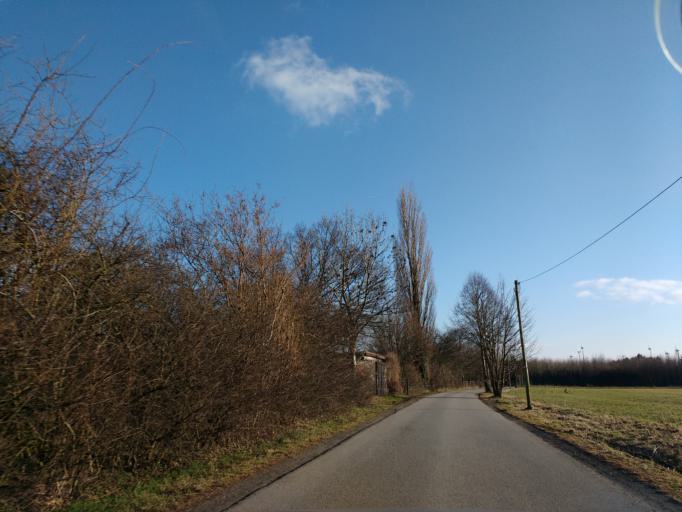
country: DE
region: North Rhine-Westphalia
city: Bad Lippspringe
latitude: 51.7535
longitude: 8.8428
